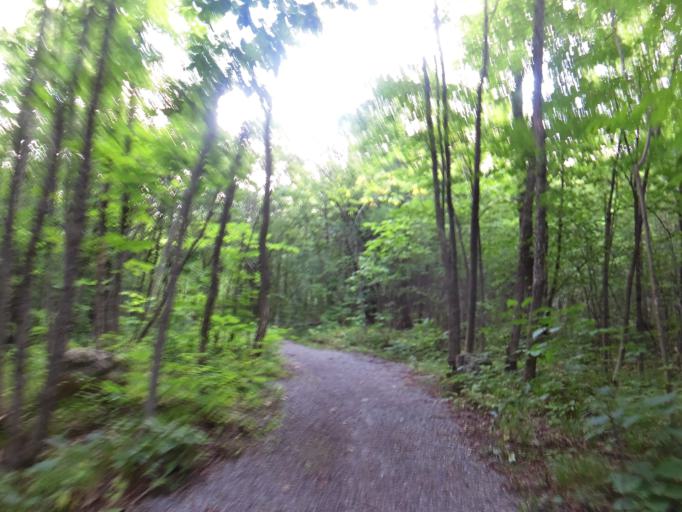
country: CA
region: Ontario
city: Bells Corners
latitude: 45.3092
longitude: -75.8148
